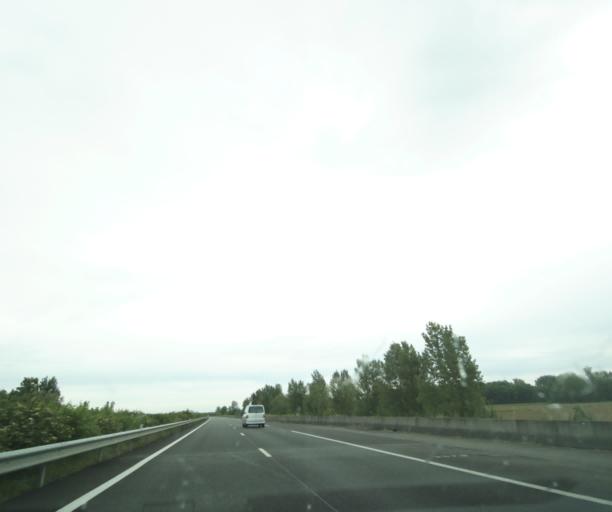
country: FR
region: Midi-Pyrenees
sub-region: Departement du Tarn-et-Garonne
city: Caussade
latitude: 44.1449
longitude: 1.5046
